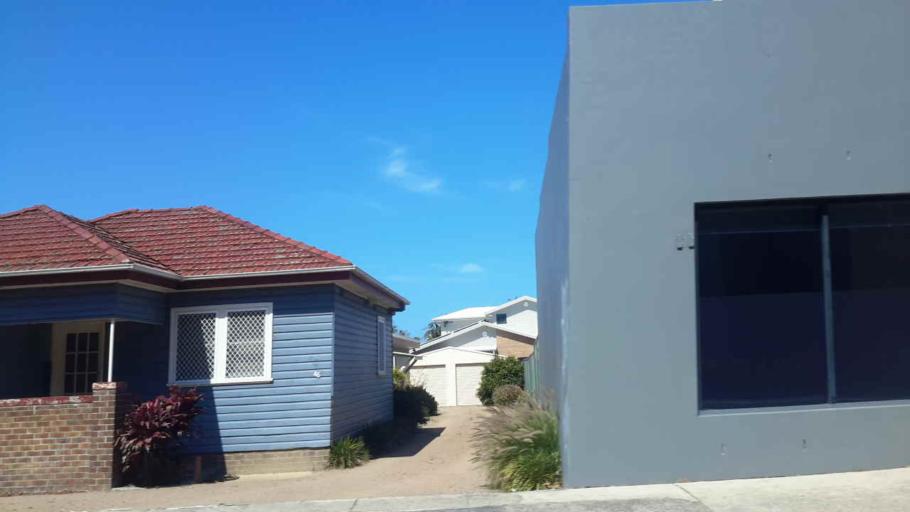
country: AU
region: New South Wales
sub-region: Wollongong
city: Fairy Meadow
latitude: -34.3903
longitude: 150.8936
